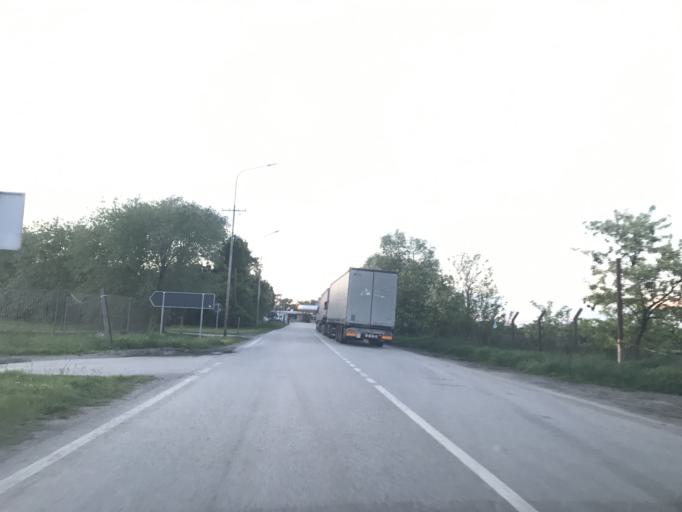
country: RS
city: Srpska Crnja
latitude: 45.7482
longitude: 20.6999
